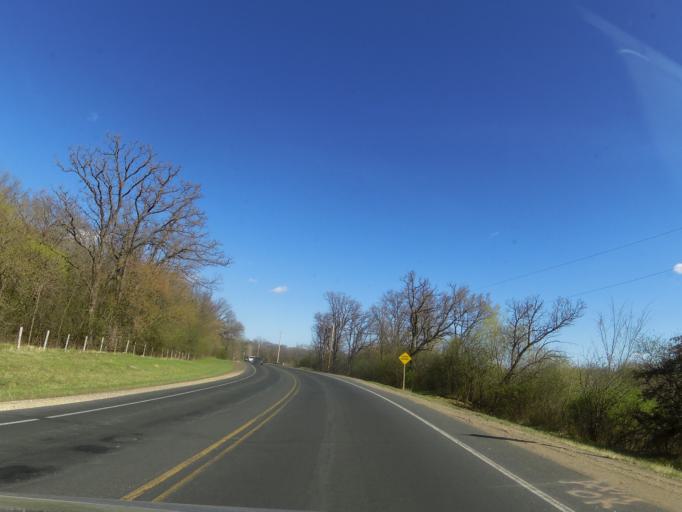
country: US
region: Wisconsin
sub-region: Saint Croix County
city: Somerset
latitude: 45.0285
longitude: -92.6643
